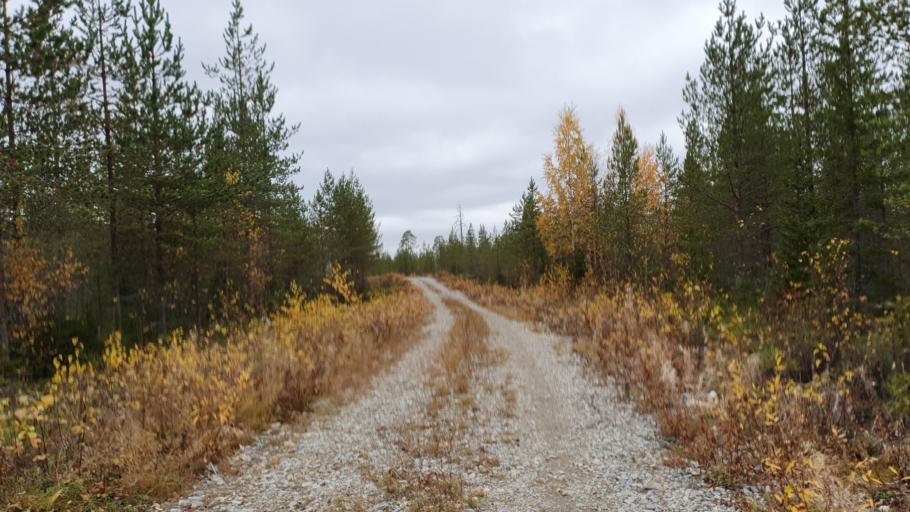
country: FI
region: Kainuu
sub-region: Kehys-Kainuu
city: Kuhmo
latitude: 64.4505
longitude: 29.5972
